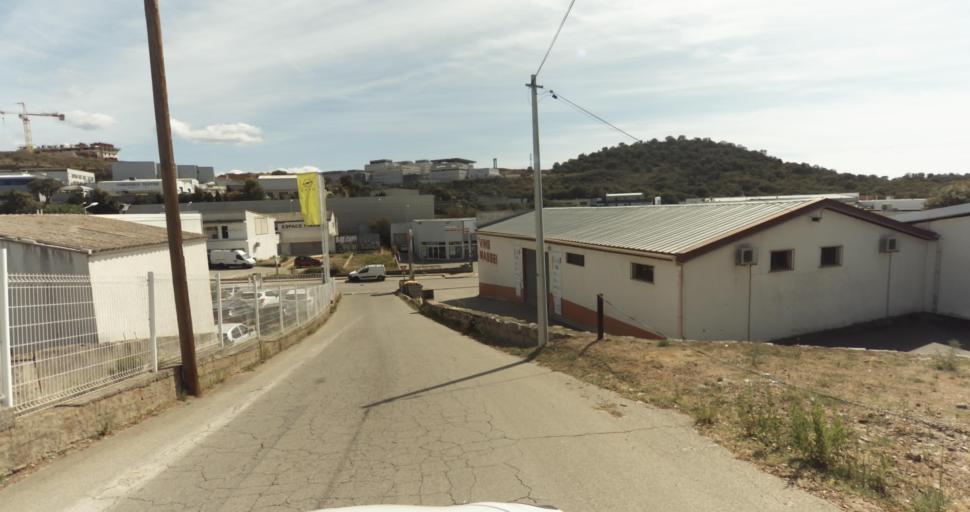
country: FR
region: Corsica
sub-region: Departement de la Corse-du-Sud
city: Alata
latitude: 41.9493
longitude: 8.7664
